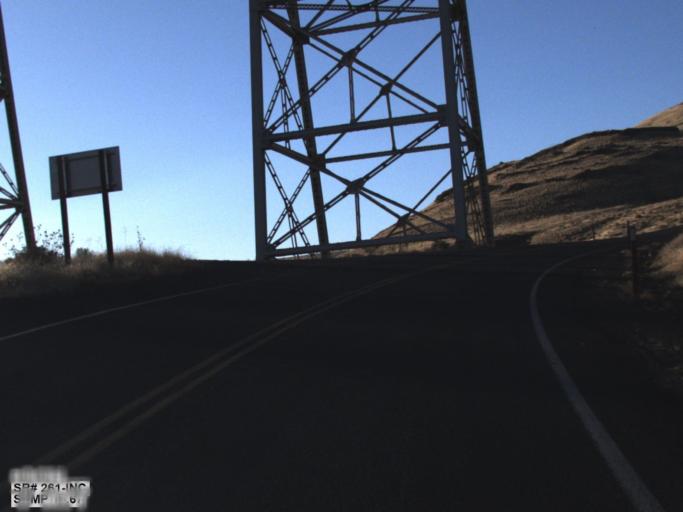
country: US
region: Washington
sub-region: Walla Walla County
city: Waitsburg
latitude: 46.5983
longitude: -118.2232
